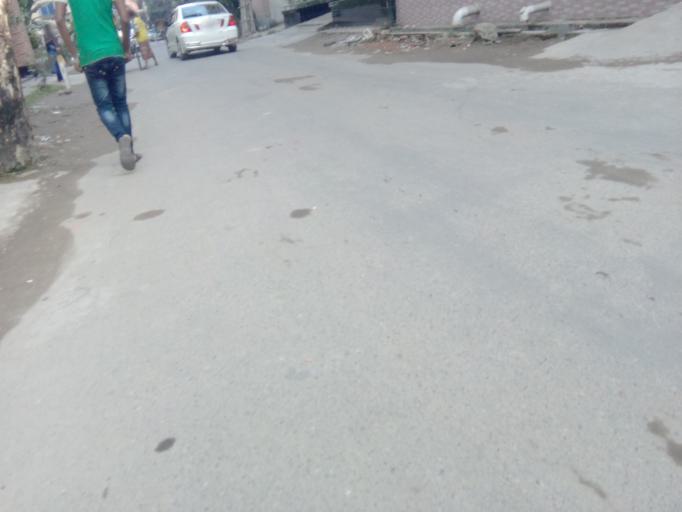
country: BD
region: Dhaka
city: Tungi
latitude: 23.8204
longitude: 90.4322
